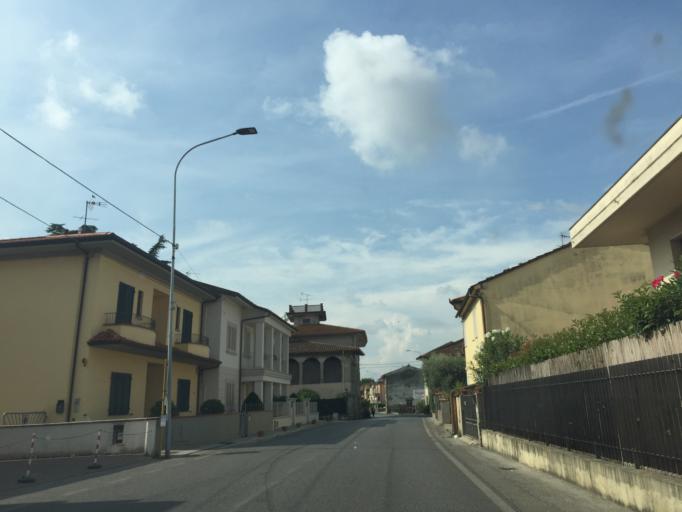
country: IT
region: Tuscany
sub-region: Provincia di Pistoia
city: Lamporecchio
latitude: 43.8034
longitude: 10.8829
